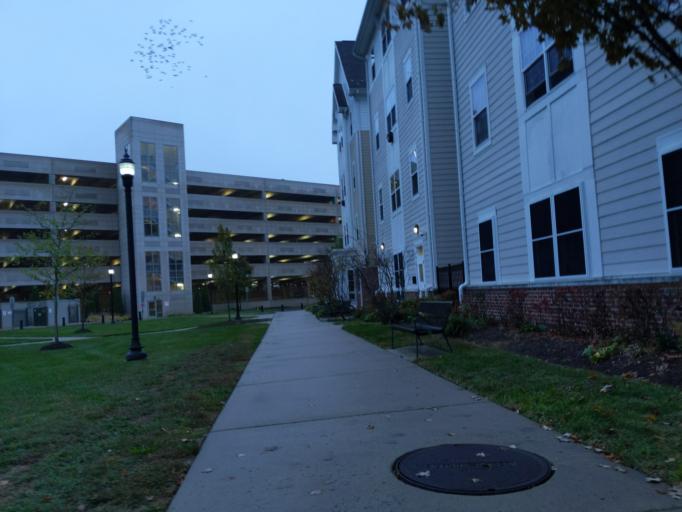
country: US
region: New Jersey
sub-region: Gloucester County
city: Glassboro
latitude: 39.7058
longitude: -75.1118
